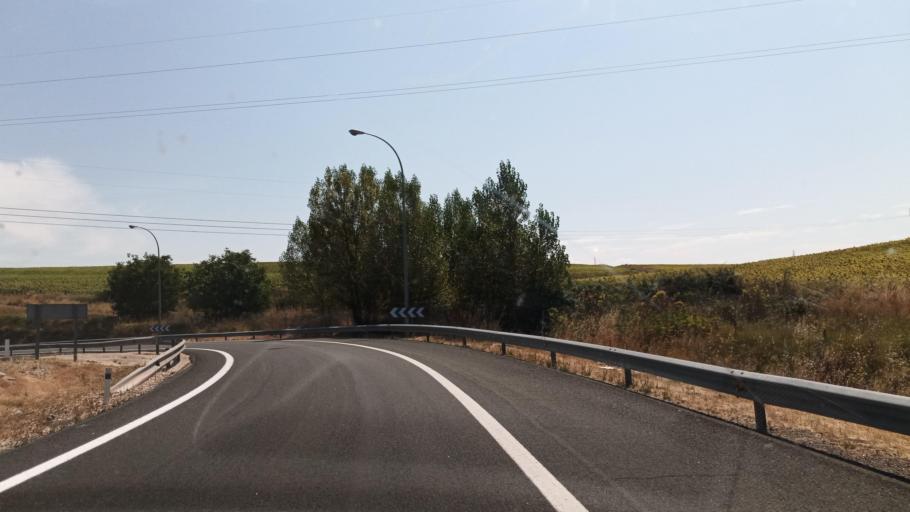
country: ES
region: Castille and Leon
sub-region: Provincia de Burgos
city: Briviesca
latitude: 42.5310
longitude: -3.3216
